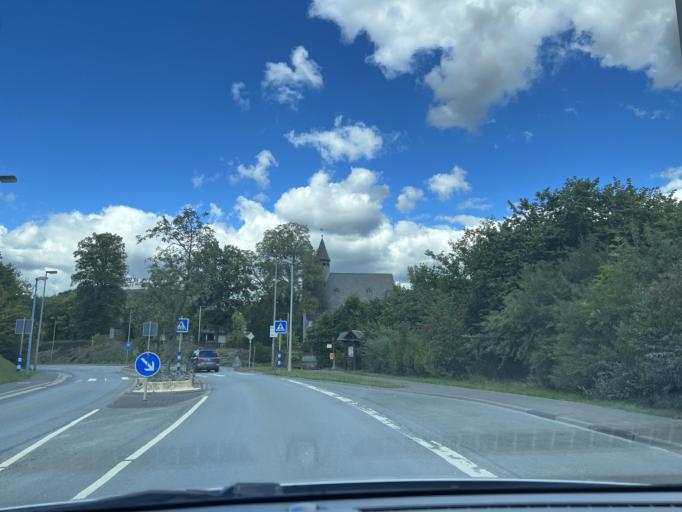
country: DE
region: North Rhine-Westphalia
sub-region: Regierungsbezirk Arnsberg
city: Bad Berleburg
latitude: 51.0279
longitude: 8.3851
